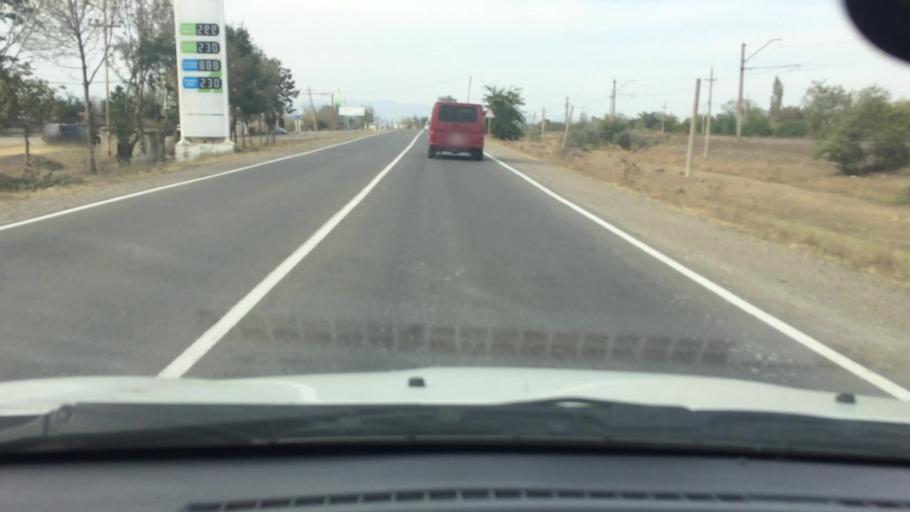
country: GE
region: Kvemo Kartli
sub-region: Marneuli
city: Marneuli
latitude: 41.4376
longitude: 44.8184
